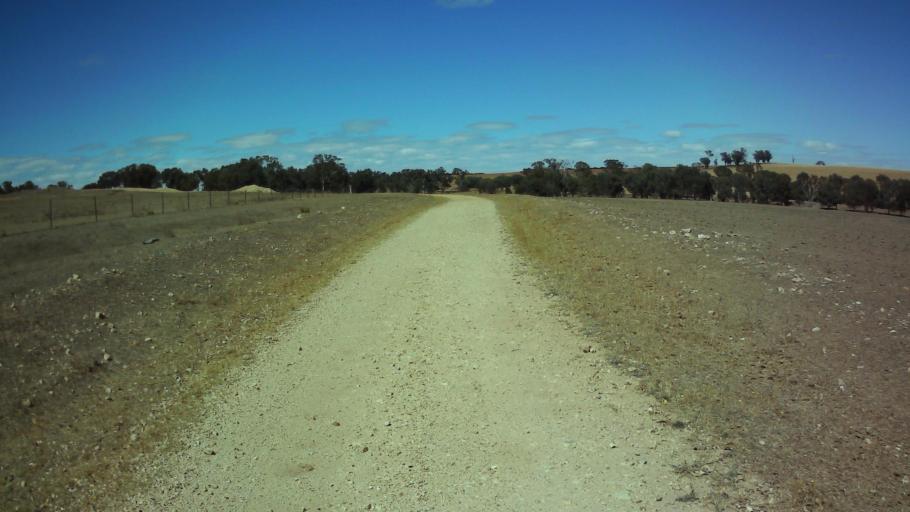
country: AU
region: New South Wales
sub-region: Young
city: Young
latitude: -34.0414
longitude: 148.4296
